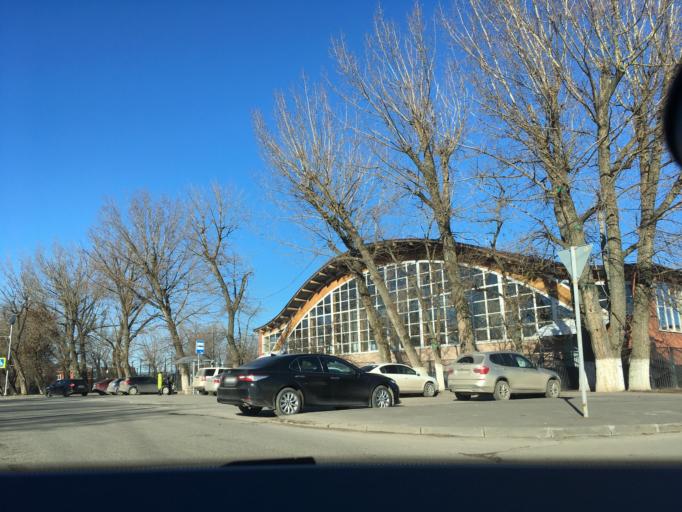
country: RU
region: Rostov
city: Imeni Chkalova
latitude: 47.2704
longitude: 39.7929
